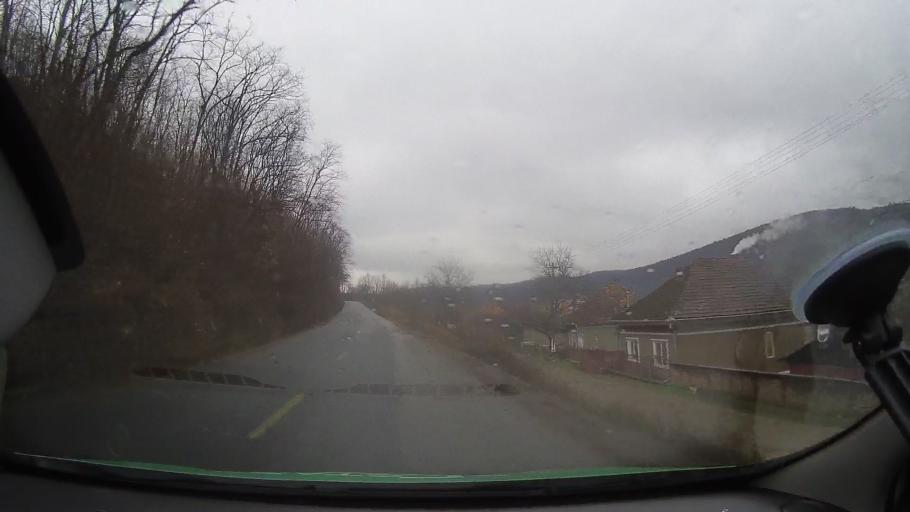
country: RO
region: Arad
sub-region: Comuna Halmagiu
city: Halmagiu
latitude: 46.2374
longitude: 22.5580
